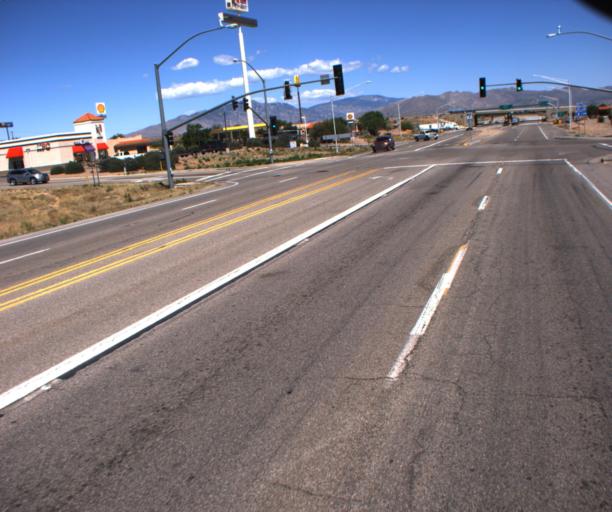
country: US
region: Arizona
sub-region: Cochise County
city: Whetstone
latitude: 31.9613
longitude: -110.3451
